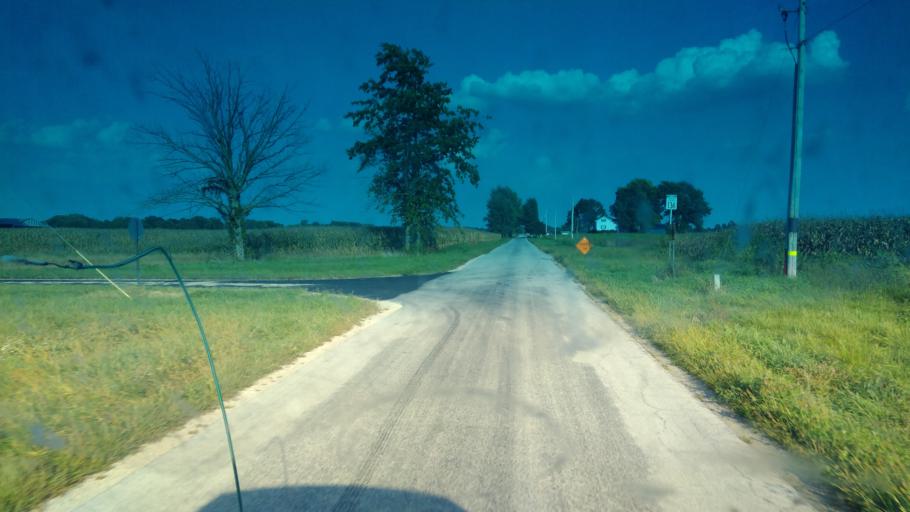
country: US
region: Ohio
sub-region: Wyandot County
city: Upper Sandusky
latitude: 40.9353
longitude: -83.1461
